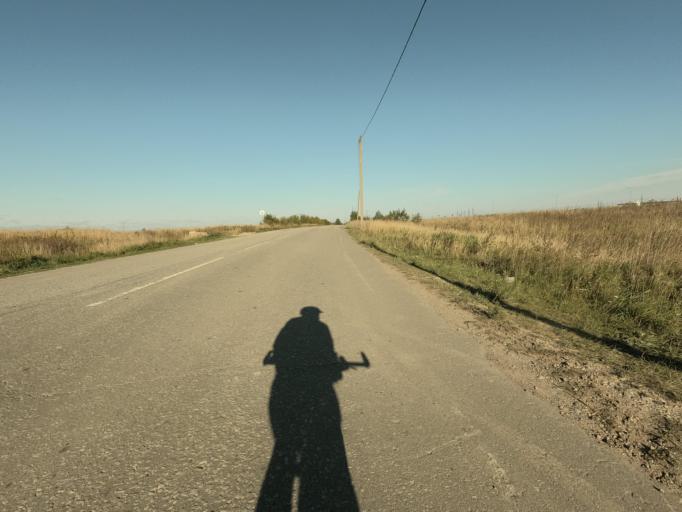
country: RU
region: St.-Petersburg
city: Petro-Slavyanka
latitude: 59.7691
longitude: 30.4934
